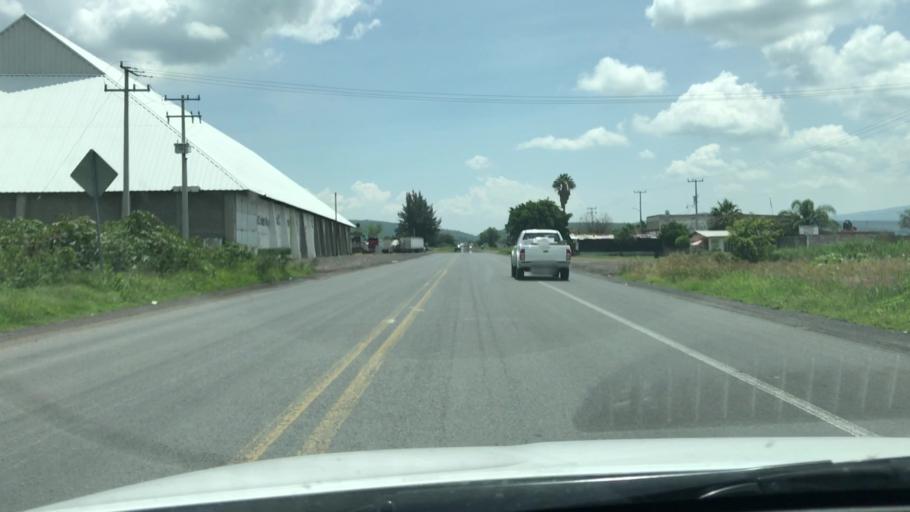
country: MX
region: Michoacan
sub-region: Yurecuaro
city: Yurecuaro
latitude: 20.3236
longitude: -102.2796
